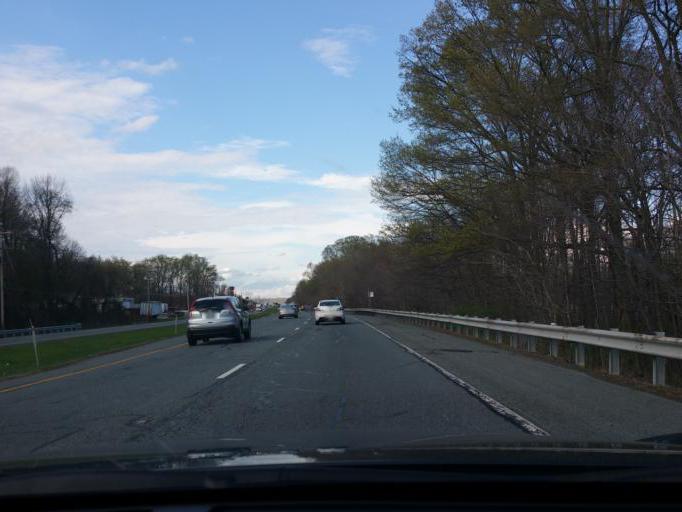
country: US
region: Maryland
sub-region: Harford County
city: Havre de Grace
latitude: 39.5381
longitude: -76.1126
